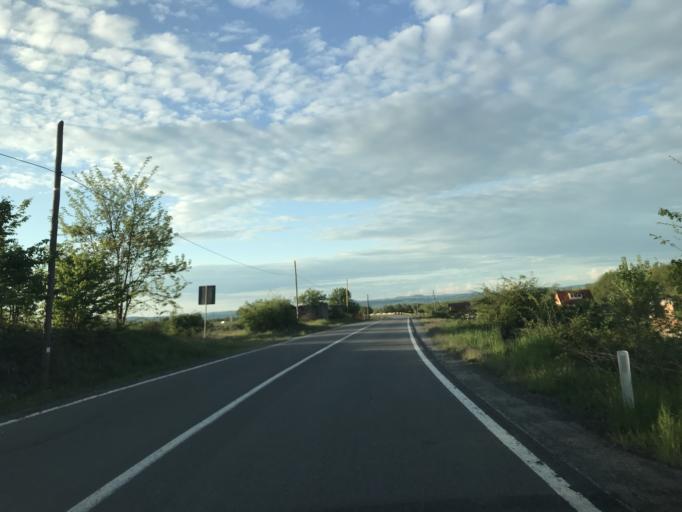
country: RO
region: Sibiu
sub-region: Comuna Cartisoara
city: Cartisoara
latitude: 45.7027
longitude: 24.5711
